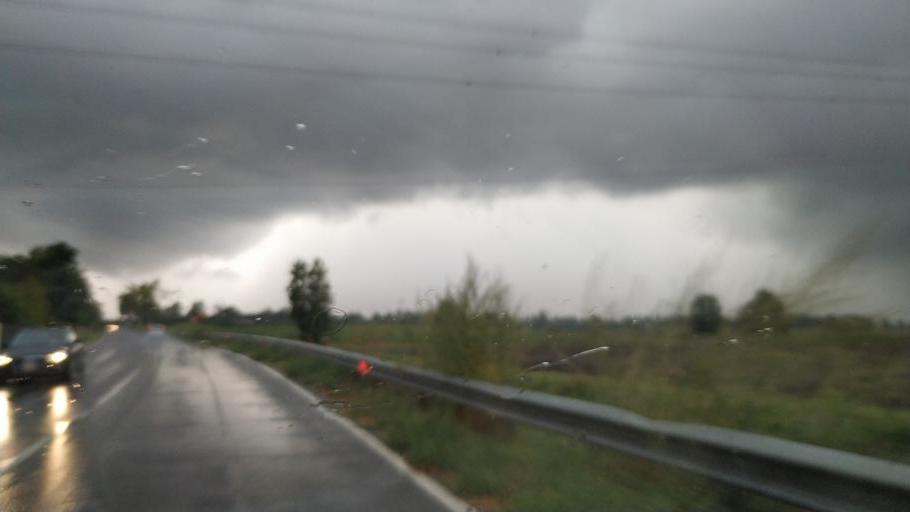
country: IT
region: Emilia-Romagna
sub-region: Provincia di Ferrara
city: Pontegradella
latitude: 44.8527
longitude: 11.6709
